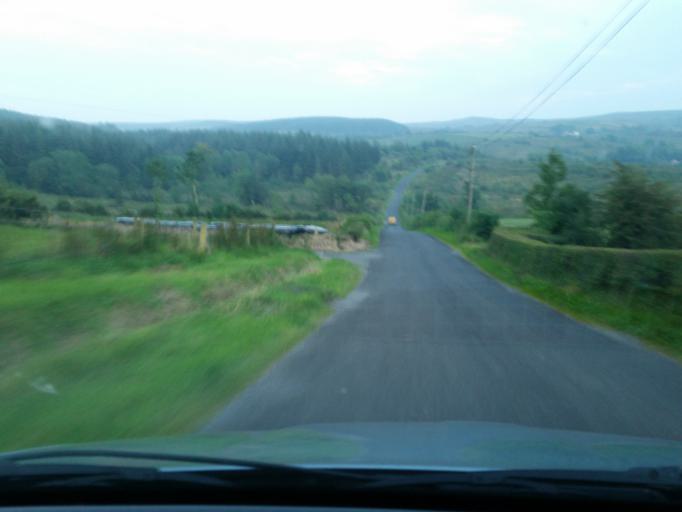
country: GB
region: Northern Ireland
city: Fivemiletown
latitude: 54.2957
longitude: -7.2848
